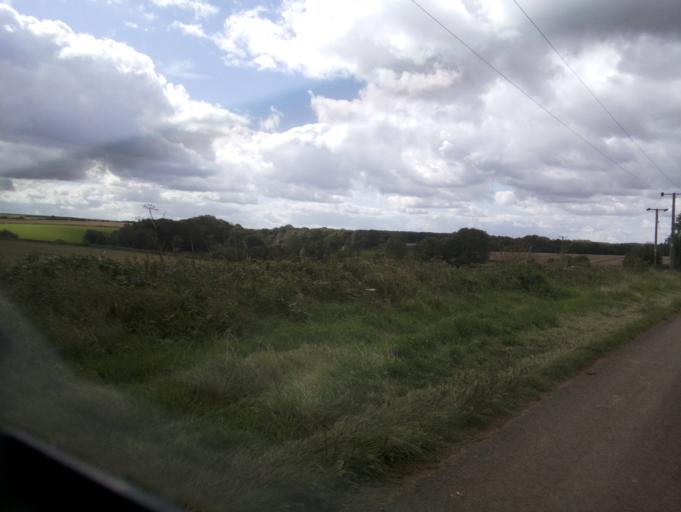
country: GB
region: England
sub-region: South Gloucestershire
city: Marshfield
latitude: 51.4918
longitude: -2.3118
